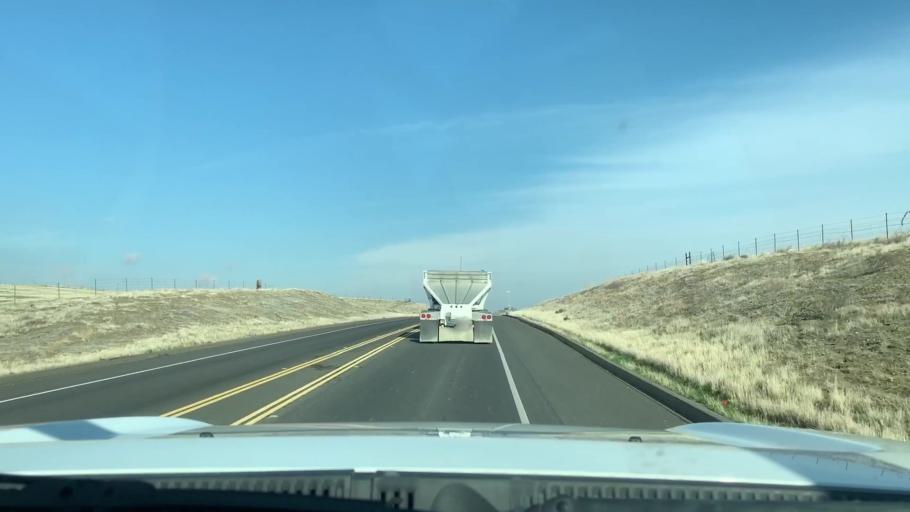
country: US
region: California
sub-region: Fresno County
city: Coalinga
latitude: 36.2133
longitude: -120.3111
